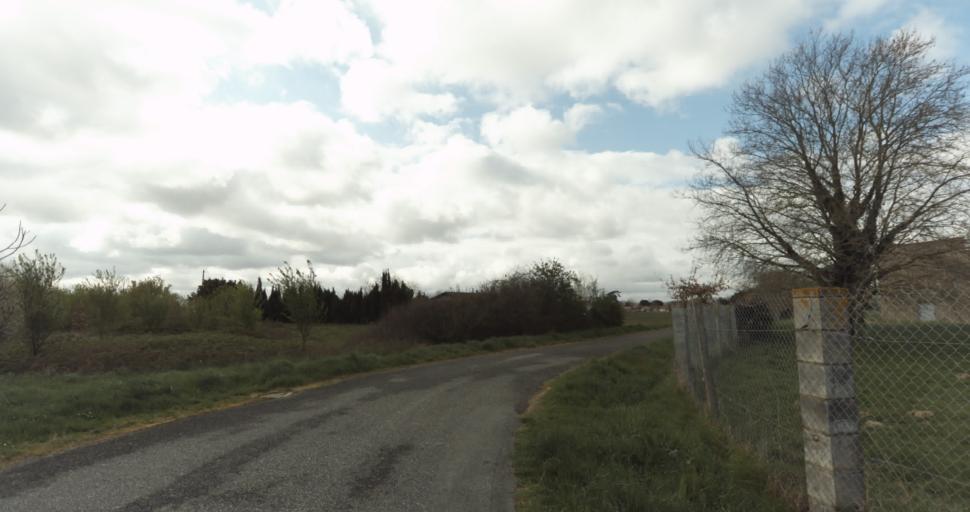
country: FR
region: Midi-Pyrenees
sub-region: Departement de la Haute-Garonne
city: Auterive
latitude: 43.3593
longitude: 1.4622
